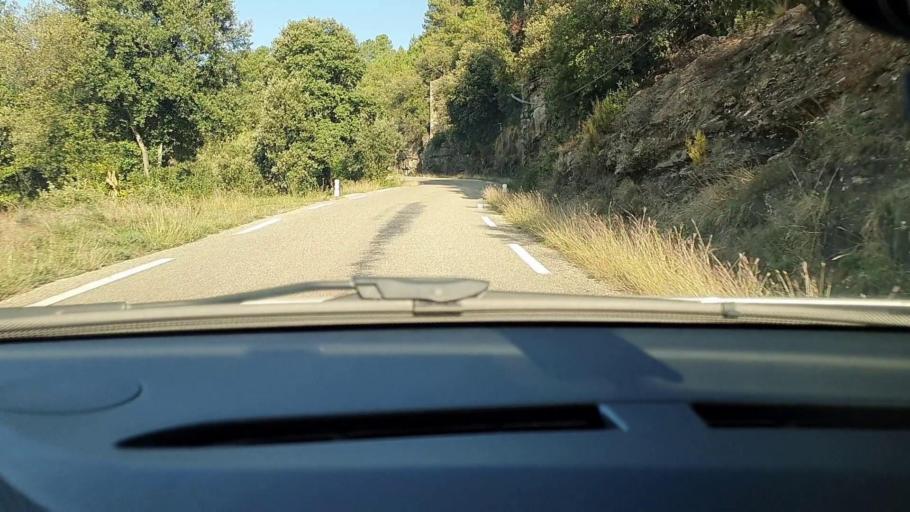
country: FR
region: Languedoc-Roussillon
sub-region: Departement du Gard
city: Besseges
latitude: 44.3089
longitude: 4.0794
